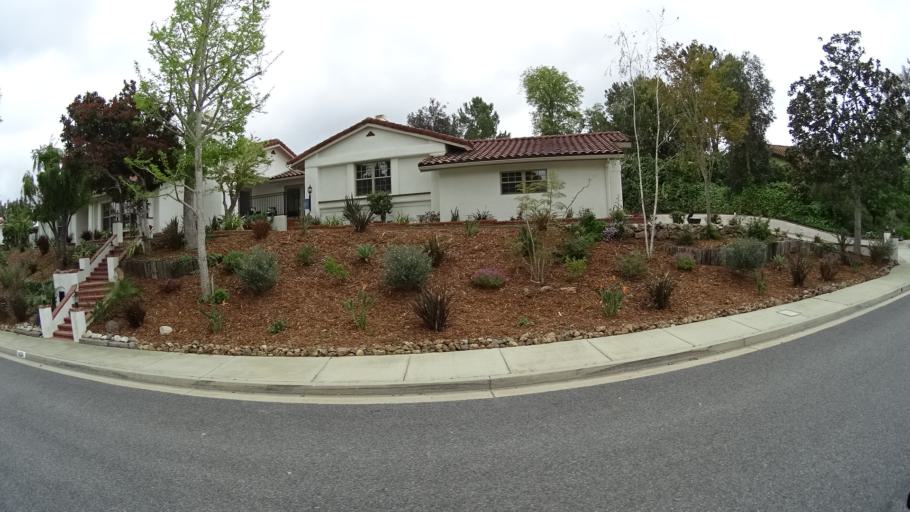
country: US
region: California
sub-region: Ventura County
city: Casa Conejo
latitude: 34.2264
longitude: -118.9025
